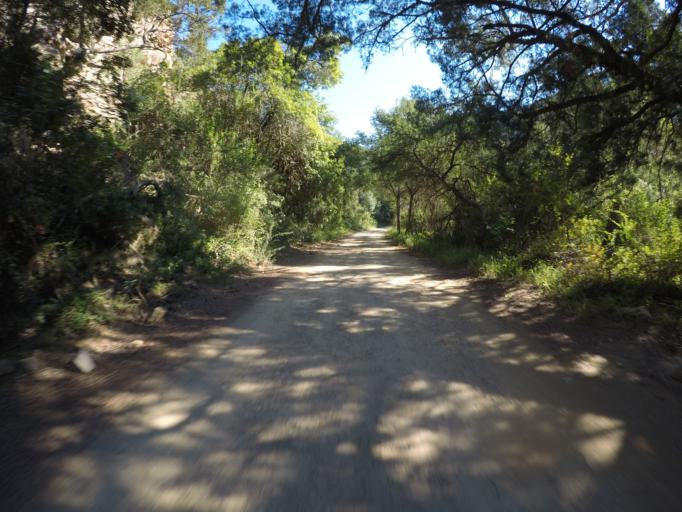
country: ZA
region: Eastern Cape
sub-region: Cacadu District Municipality
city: Kareedouw
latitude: -33.6611
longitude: 24.5354
